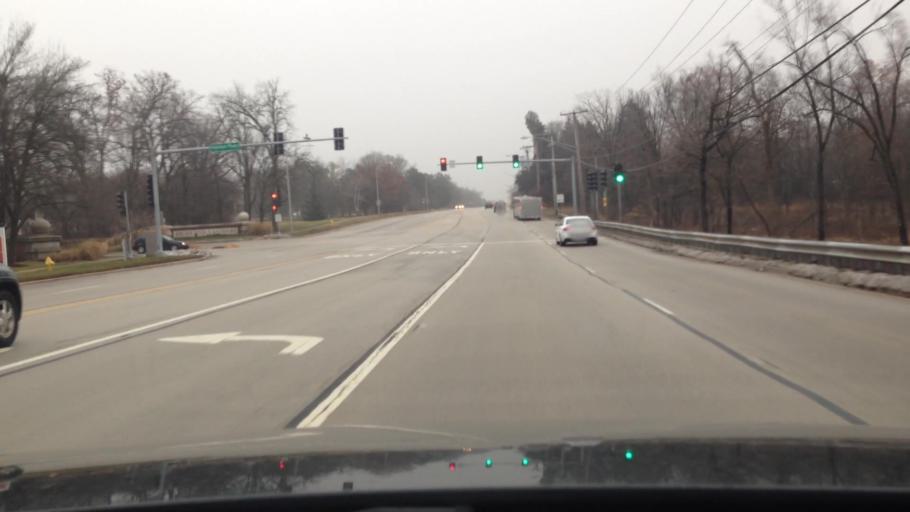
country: US
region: Illinois
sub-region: DuPage County
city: Downers Grove
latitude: 41.8311
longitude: -88.0066
